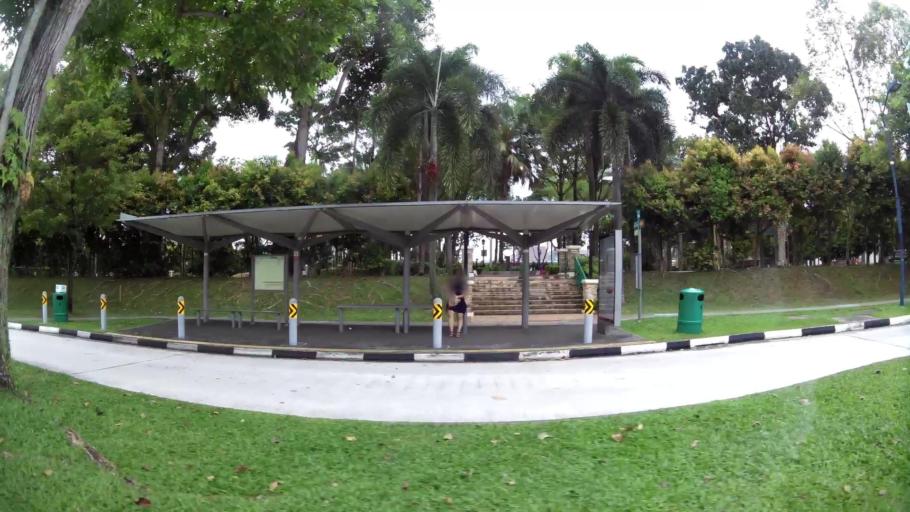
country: SG
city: Singapore
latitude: 1.3597
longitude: 103.8635
